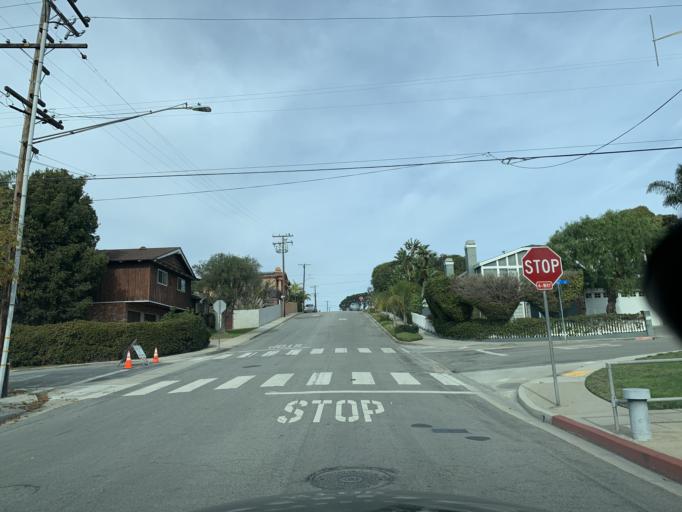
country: US
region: California
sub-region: Los Angeles County
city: Manhattan Beach
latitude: 33.8844
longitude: -118.3917
